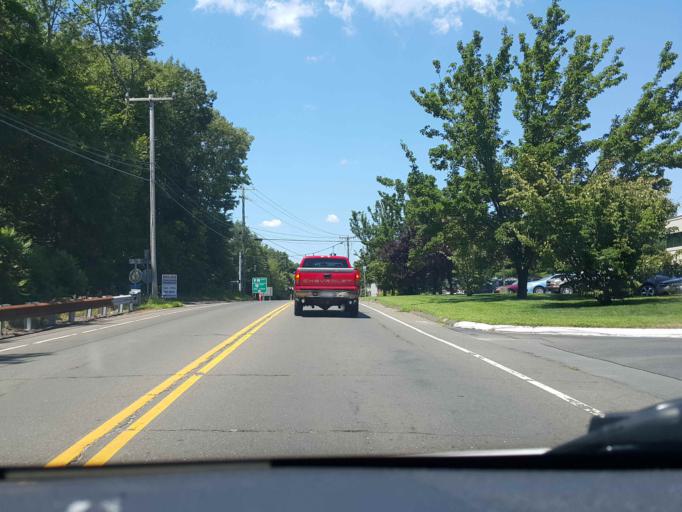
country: US
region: Connecticut
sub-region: New Haven County
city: Guilford
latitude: 41.2951
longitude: -72.7015
